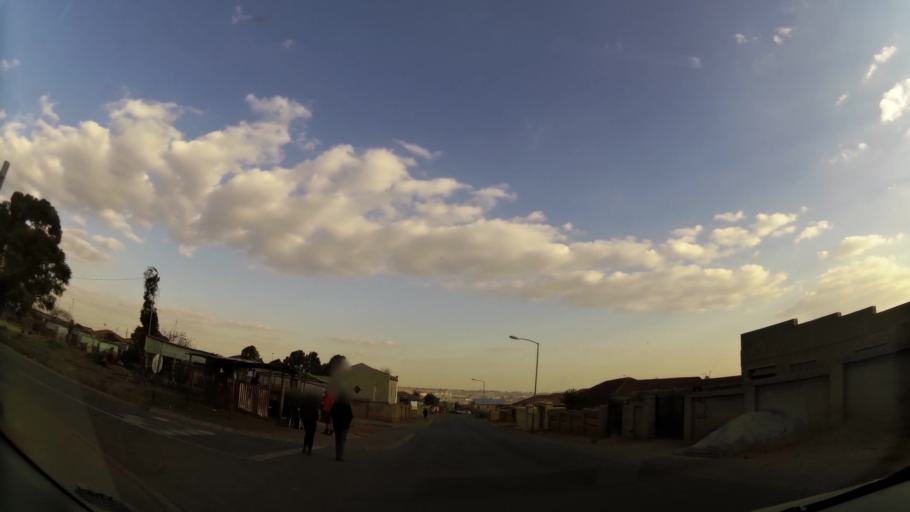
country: ZA
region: Gauteng
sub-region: West Rand District Municipality
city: Krugersdorp
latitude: -26.0749
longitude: 27.7583
